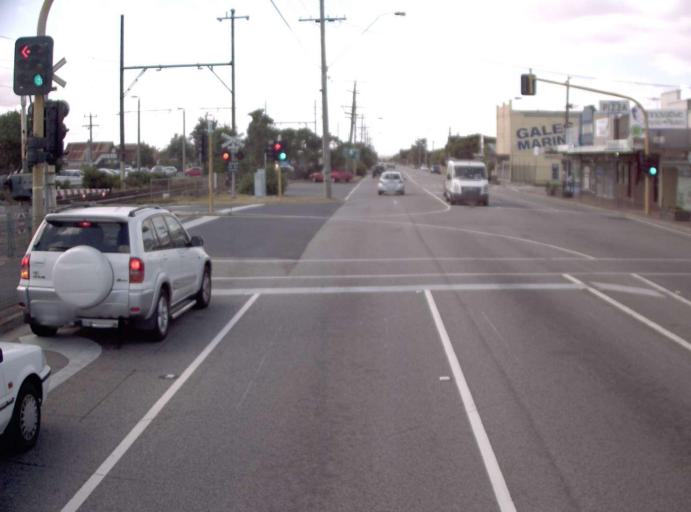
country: AU
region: Victoria
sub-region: Kingston
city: Edithvale
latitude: -38.0384
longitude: 145.1085
